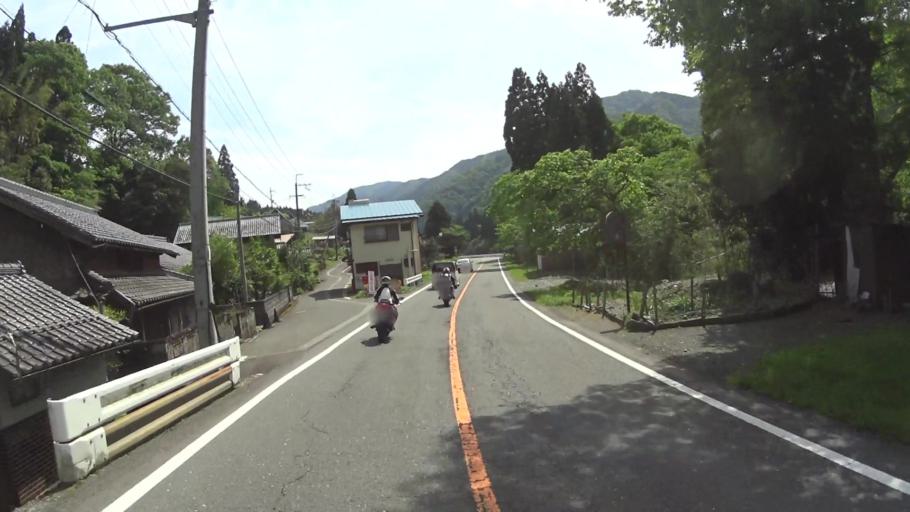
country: JP
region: Shiga Prefecture
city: Kitahama
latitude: 35.3122
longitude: 135.8954
